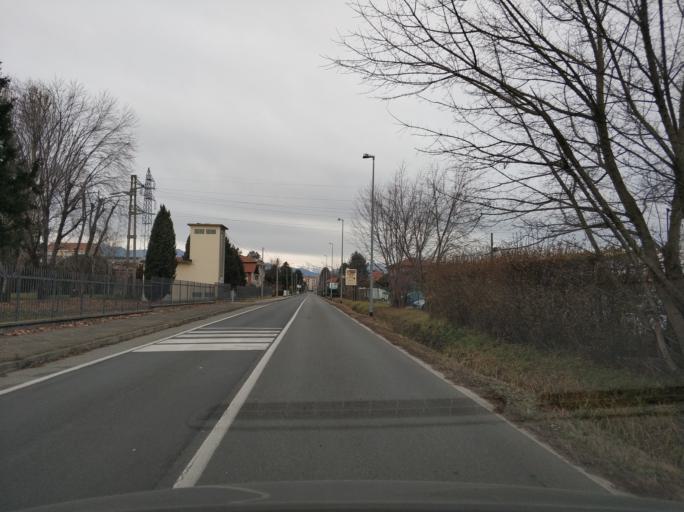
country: IT
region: Piedmont
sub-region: Provincia di Torino
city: San Maurizio
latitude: 45.2091
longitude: 7.6353
